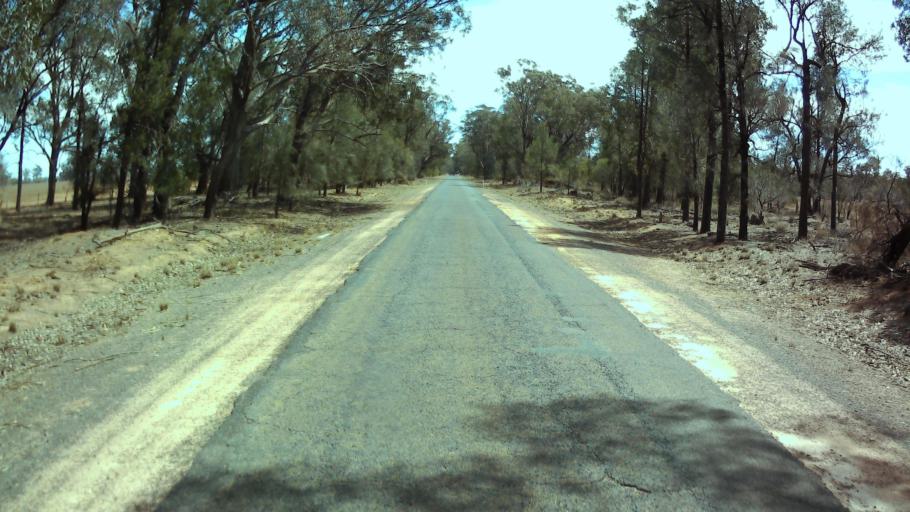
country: AU
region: New South Wales
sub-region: Weddin
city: Grenfell
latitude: -33.6499
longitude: 148.1941
